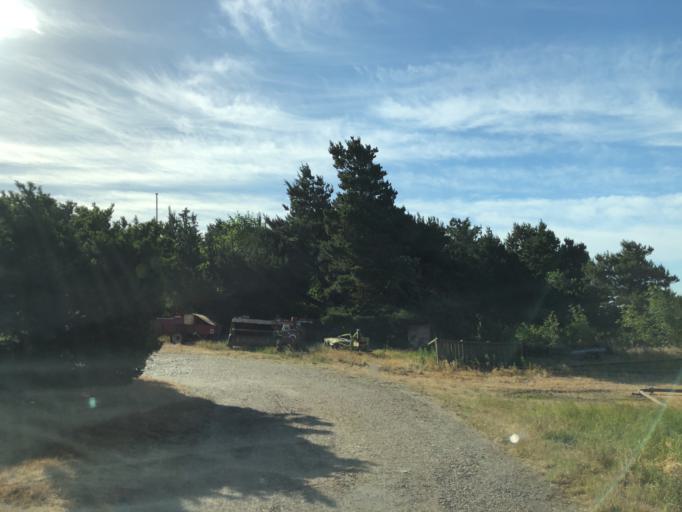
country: DK
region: Central Jutland
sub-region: Holstebro Kommune
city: Ulfborg
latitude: 56.3306
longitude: 8.2764
